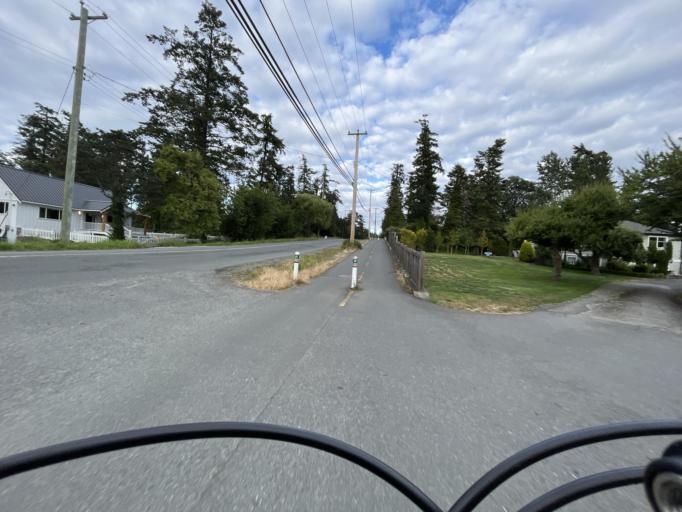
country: CA
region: British Columbia
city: Victoria
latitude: 48.4771
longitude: -123.3511
